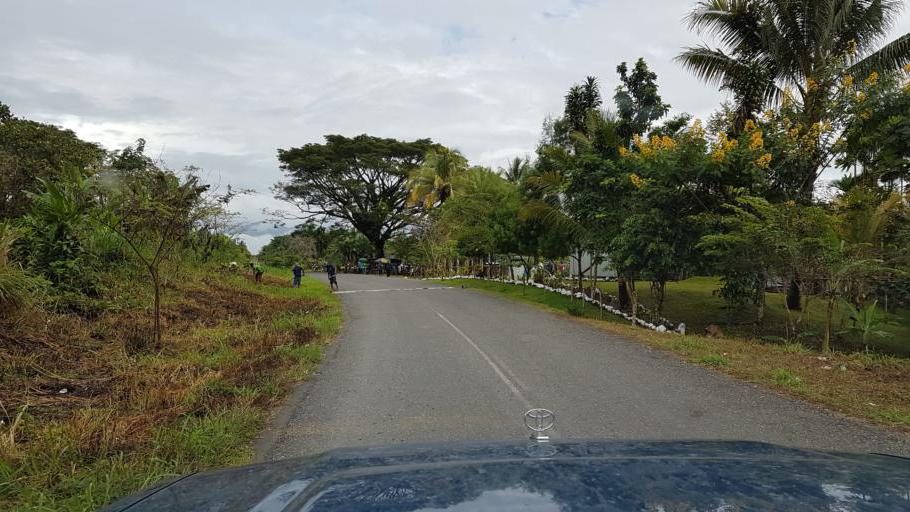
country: PG
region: Northern Province
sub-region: Sohe
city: Popondetta
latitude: -8.8303
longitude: 148.0558
